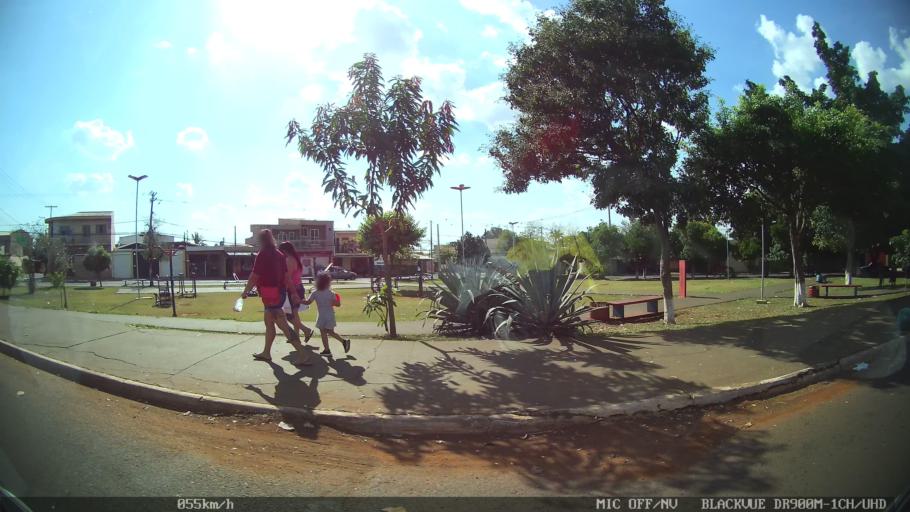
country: BR
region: Sao Paulo
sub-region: Ribeirao Preto
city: Ribeirao Preto
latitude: -21.2029
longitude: -47.8495
